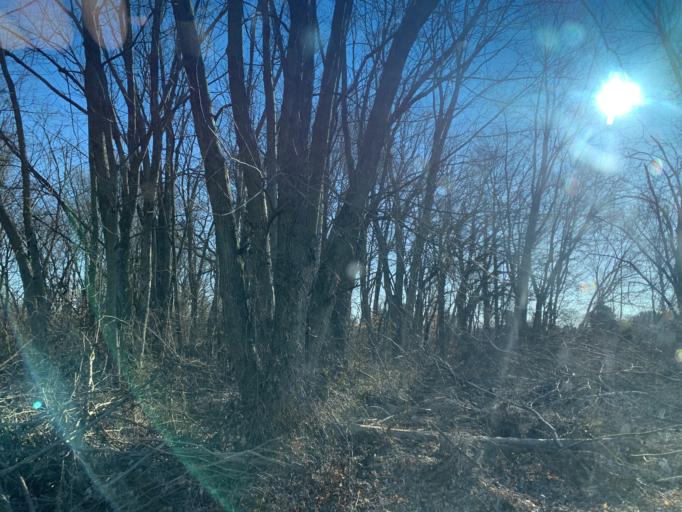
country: US
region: Maryland
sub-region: Harford County
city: Aberdeen
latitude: 39.5758
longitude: -76.2014
